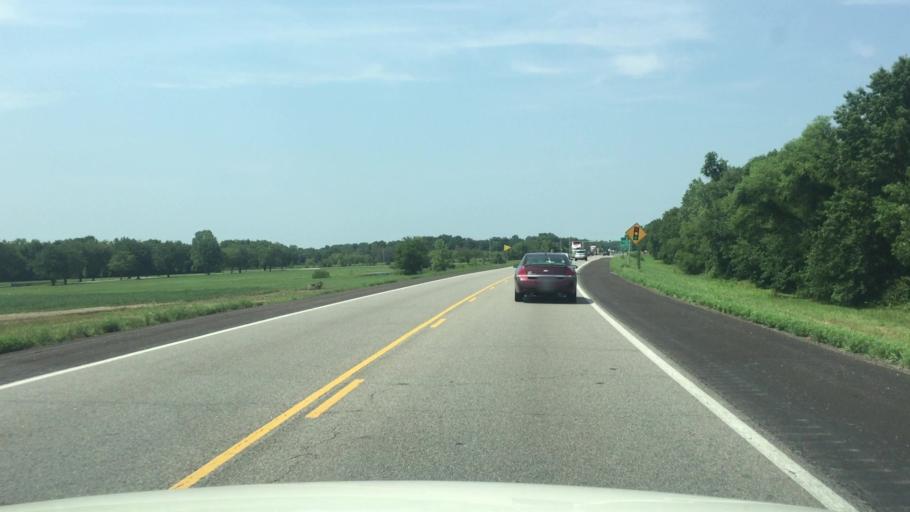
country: US
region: Kansas
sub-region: Crawford County
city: Pittsburg
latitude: 37.3929
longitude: -94.7171
